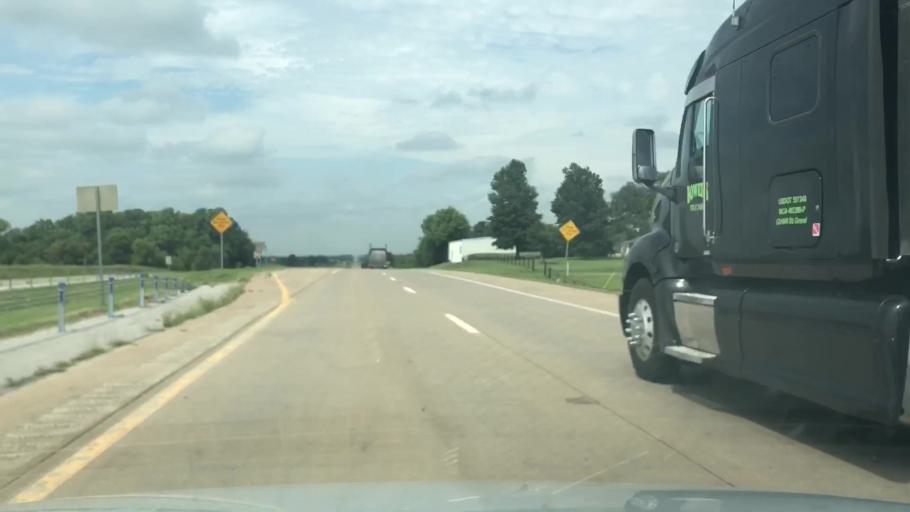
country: US
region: Oklahoma
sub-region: Washington County
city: Bartlesville
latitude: 36.6383
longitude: -95.9352
